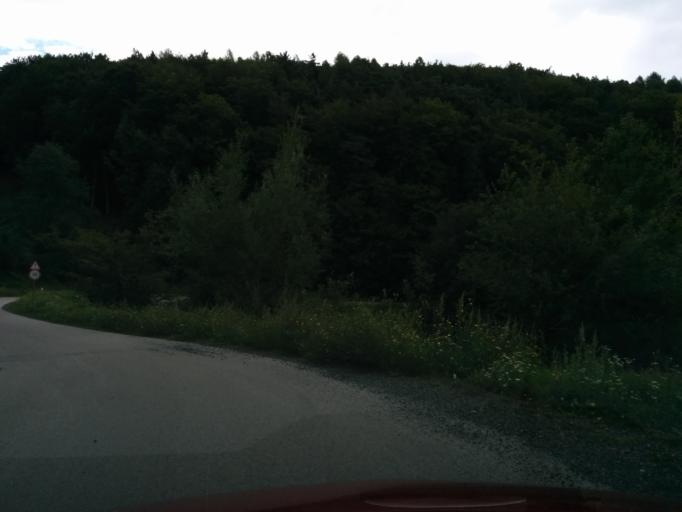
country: AT
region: Burgenland
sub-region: Politischer Bezirk Oberwart
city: Rechnitz
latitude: 47.3551
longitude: 16.4778
